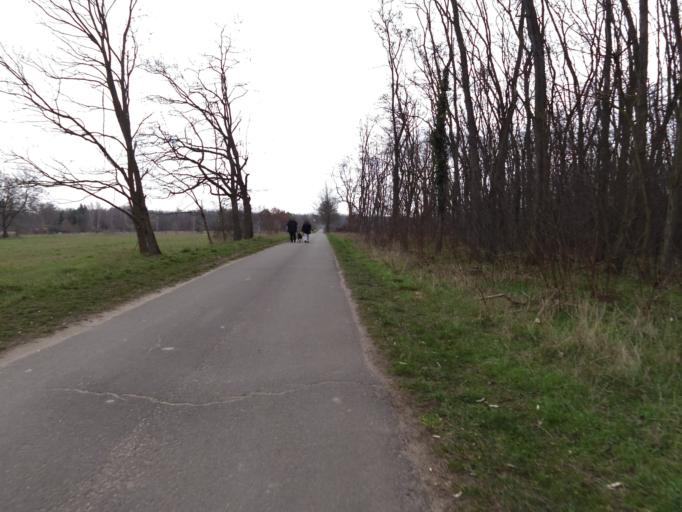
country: DE
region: Rheinland-Pfalz
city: Maxdorf
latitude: 49.4896
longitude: 8.2762
